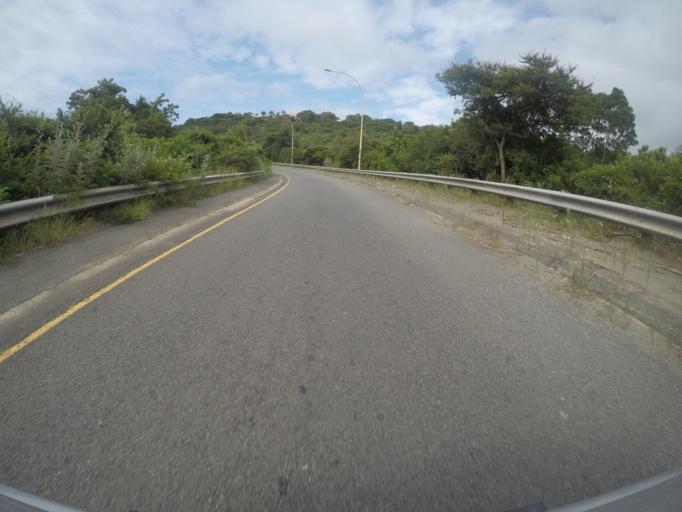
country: ZA
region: Eastern Cape
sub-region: Buffalo City Metropolitan Municipality
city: East London
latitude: -32.9764
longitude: 27.9204
